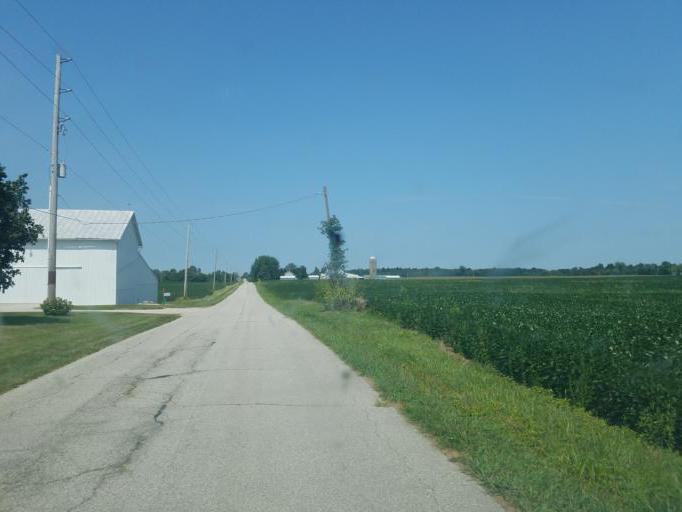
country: US
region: Ohio
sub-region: Crawford County
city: Bucyrus
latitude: 40.8583
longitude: -83.1123
